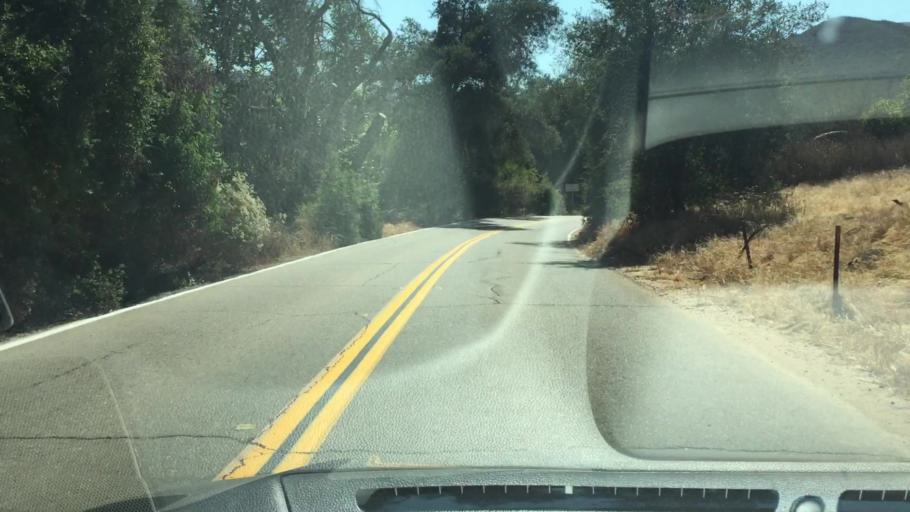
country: US
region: California
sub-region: San Diego County
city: Alpine
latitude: 32.7541
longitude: -116.7807
